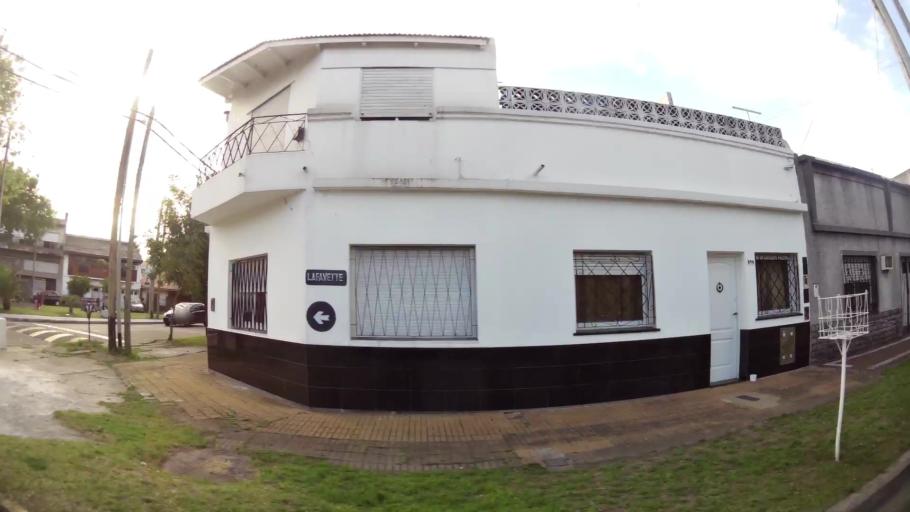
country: AR
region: Buenos Aires
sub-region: Partido de Avellaneda
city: Avellaneda
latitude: -34.6750
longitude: -58.3598
